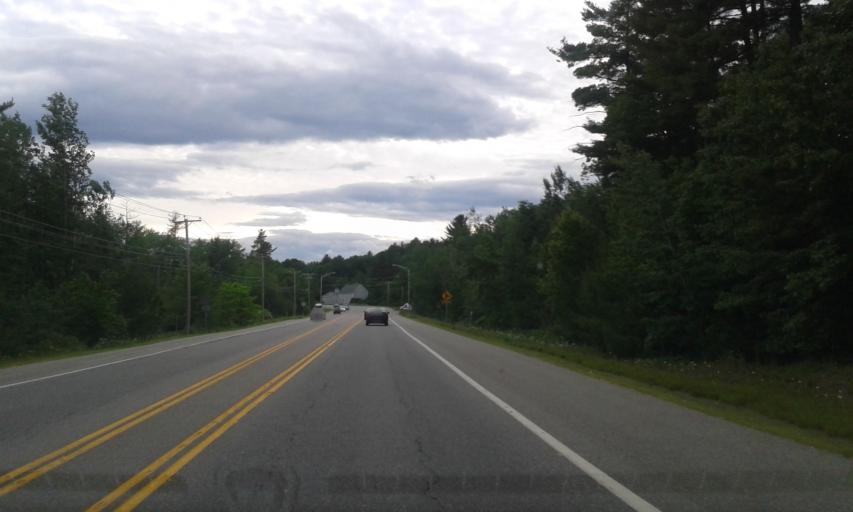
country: US
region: New Hampshire
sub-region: Hillsborough County
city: Litchfield
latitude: 42.8071
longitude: -71.5389
